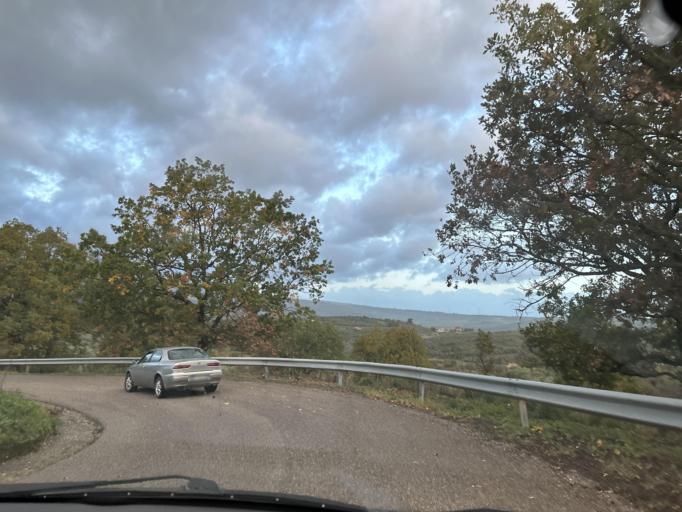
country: IT
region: Calabria
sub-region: Provincia di Catanzaro
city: Squillace
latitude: 38.7700
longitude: 16.5107
